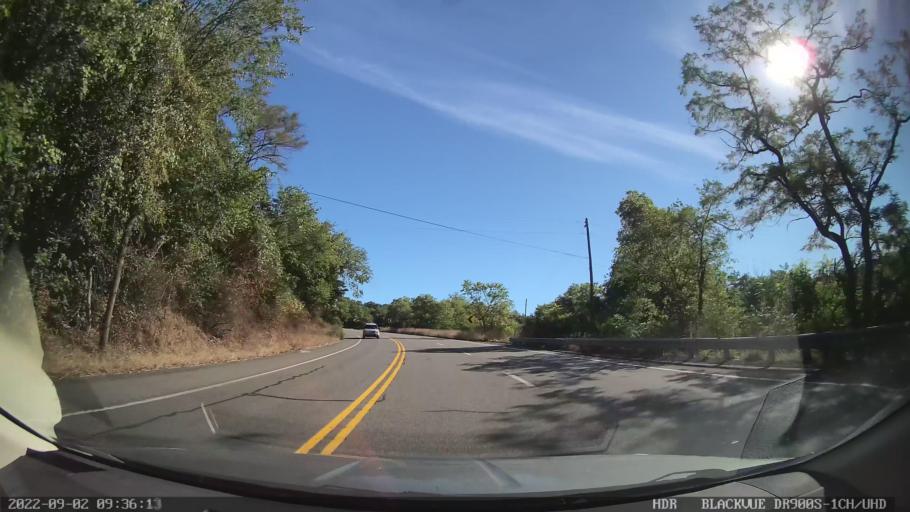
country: US
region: Pennsylvania
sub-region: Northumberland County
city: Elysburg
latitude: 40.8800
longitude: -76.5516
